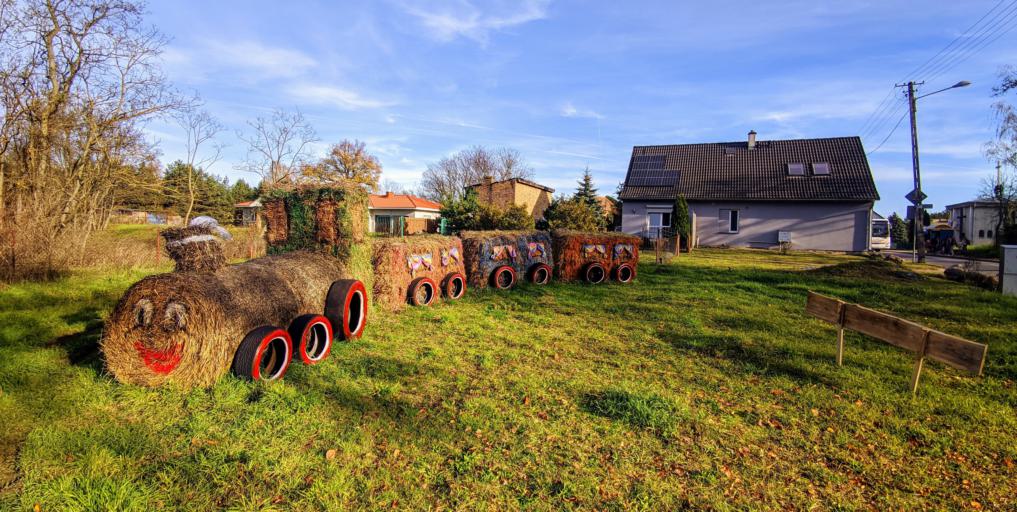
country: PL
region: Lubusz
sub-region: Powiat miedzyrzecki
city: Miedzyrzecz
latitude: 52.4041
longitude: 15.5388
